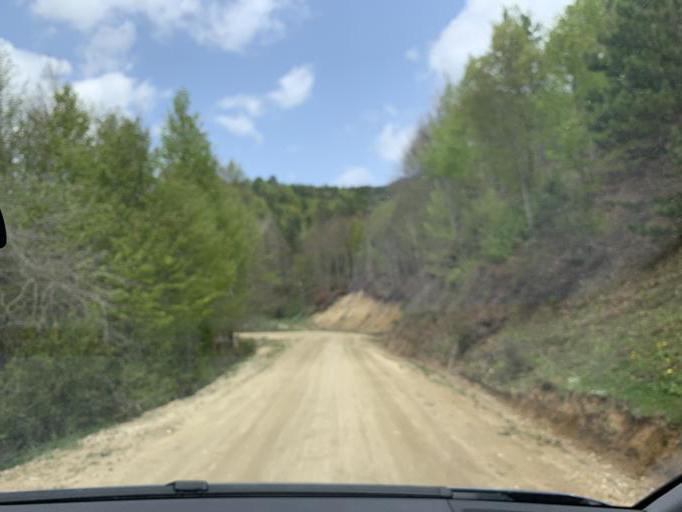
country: TR
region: Bolu
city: Bolu
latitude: 40.8336
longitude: 31.6720
